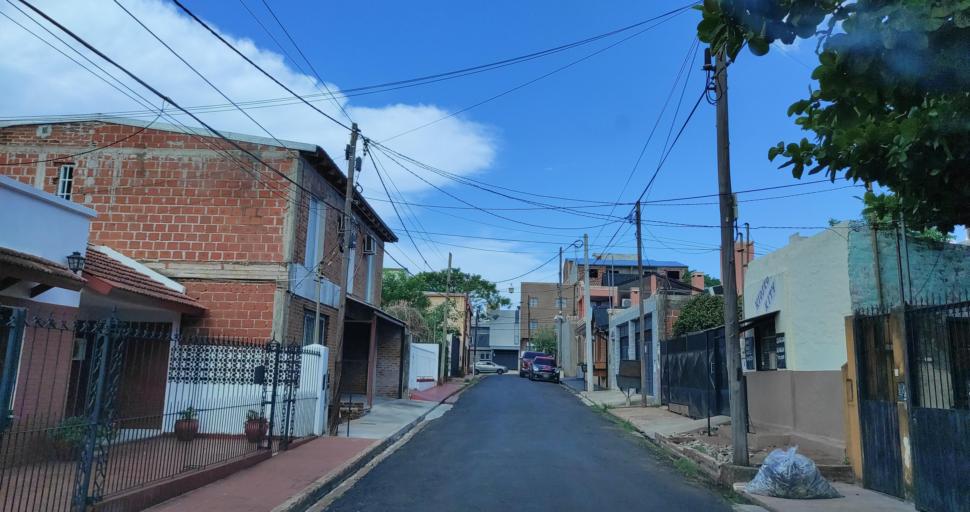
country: AR
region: Misiones
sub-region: Departamento de Capital
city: Posadas
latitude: -27.3805
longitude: -55.8888
